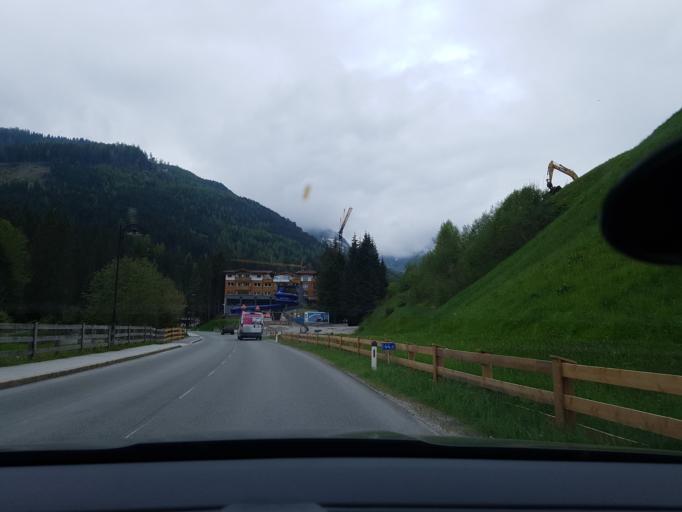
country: AT
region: Tyrol
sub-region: Politischer Bezirk Schwaz
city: Gerlos
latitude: 47.2133
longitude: 12.0065
